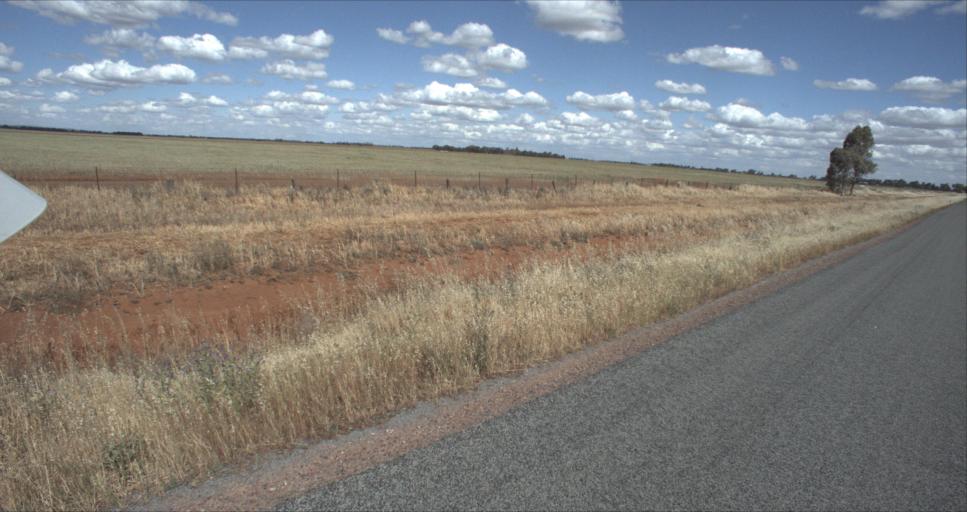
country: AU
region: New South Wales
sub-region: Leeton
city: Leeton
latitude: -34.4613
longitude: 146.2527
